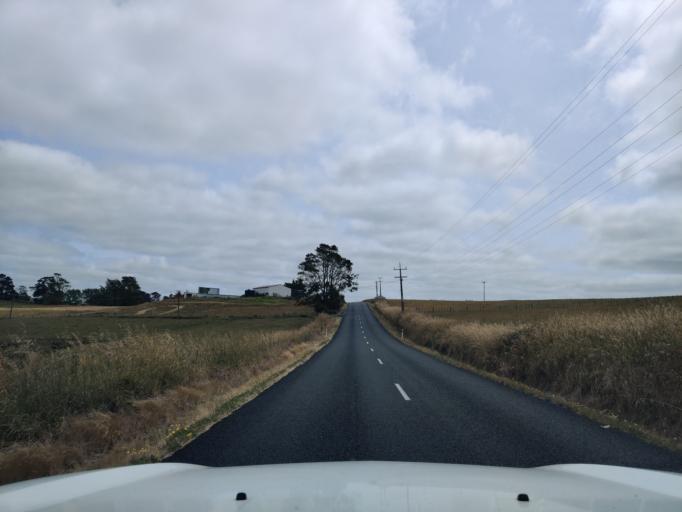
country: NZ
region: Waikato
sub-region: Waikato District
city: Te Kauwhata
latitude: -37.5103
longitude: 175.1793
